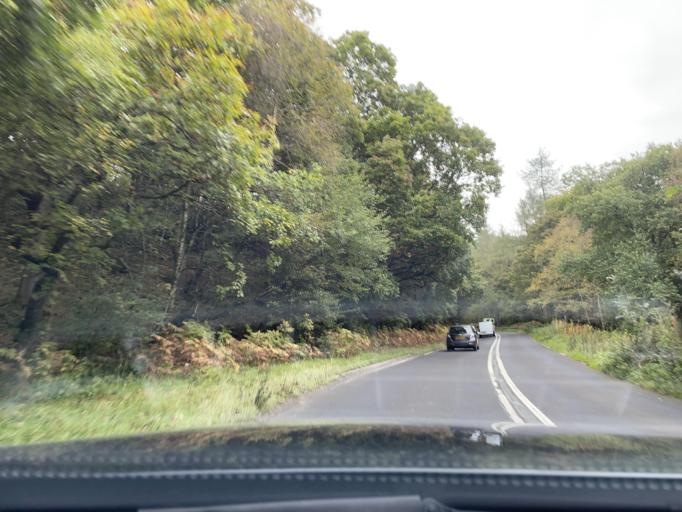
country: GB
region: England
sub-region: Derbyshire
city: Hathersage
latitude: 53.3780
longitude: -1.6862
